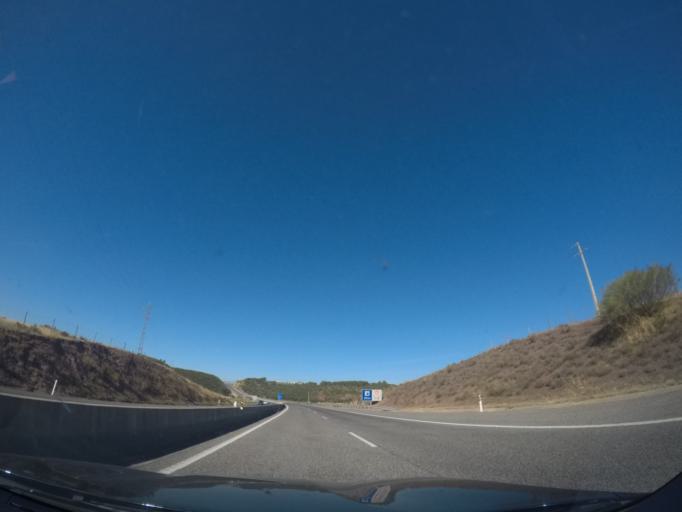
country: PT
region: Faro
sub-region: Lagos
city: Lagos
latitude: 37.1640
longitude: -8.6805
